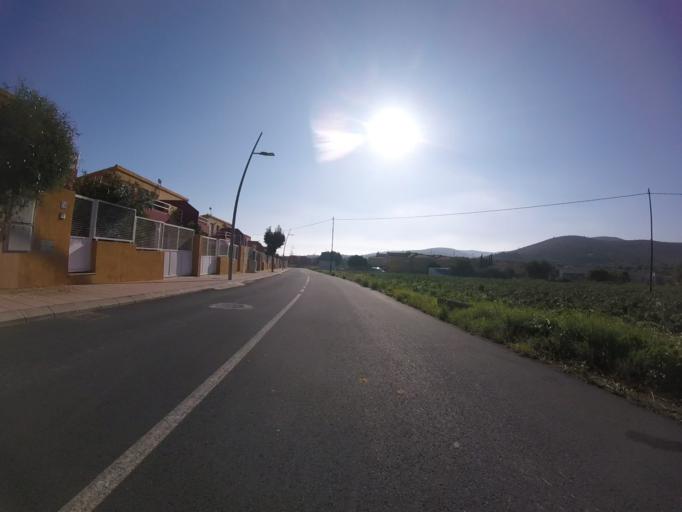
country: ES
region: Valencia
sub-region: Provincia de Castello
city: Peniscola
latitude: 40.3879
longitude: 0.3768
